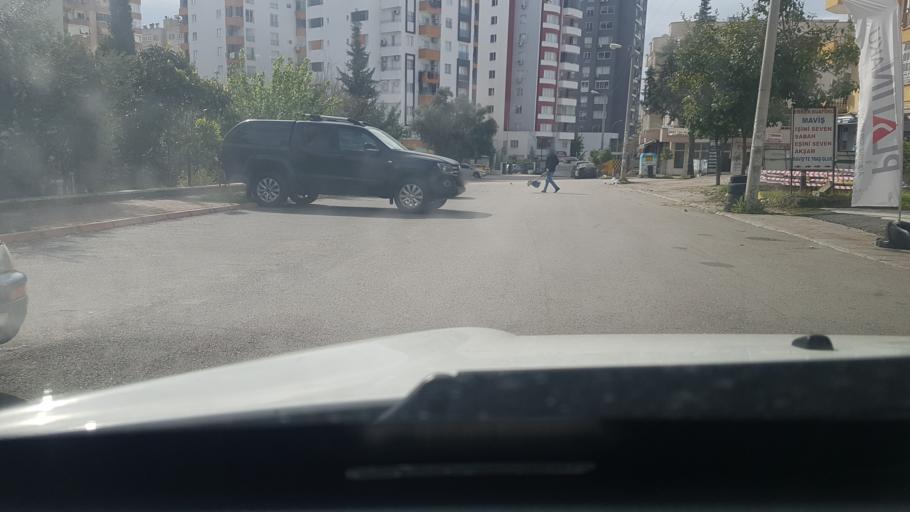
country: TR
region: Adana
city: Adana
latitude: 37.0447
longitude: 35.3022
